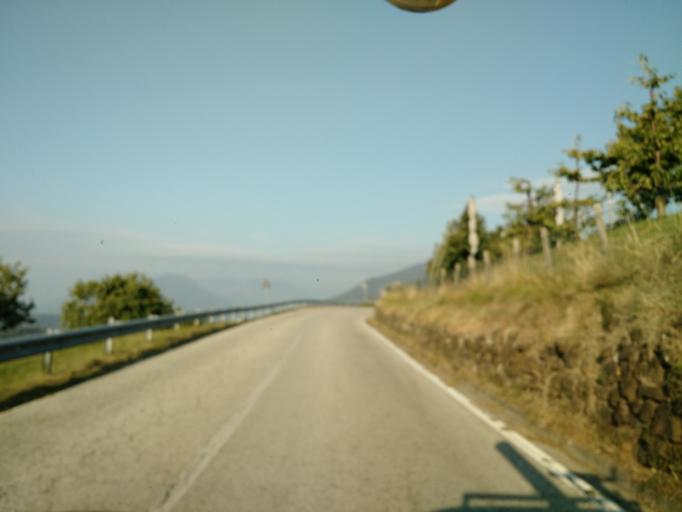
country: IT
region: Veneto
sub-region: Provincia di Vicenza
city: Salcedo
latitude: 45.7642
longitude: 11.5668
